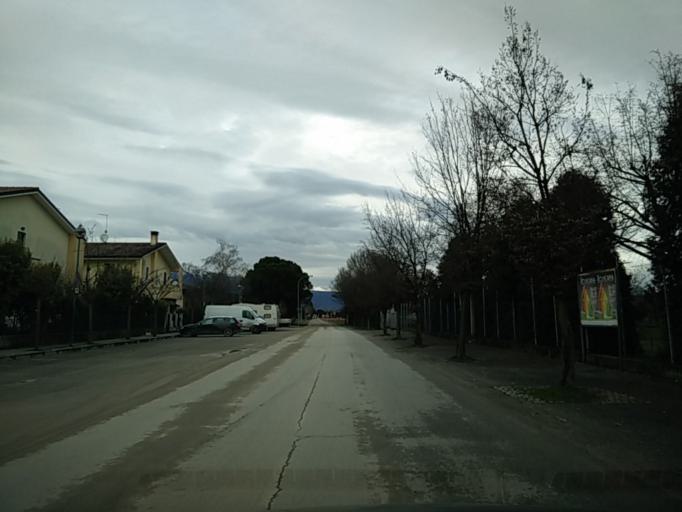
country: IT
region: Veneto
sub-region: Provincia di Treviso
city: Loria Bessica
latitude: 45.7519
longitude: 11.8792
